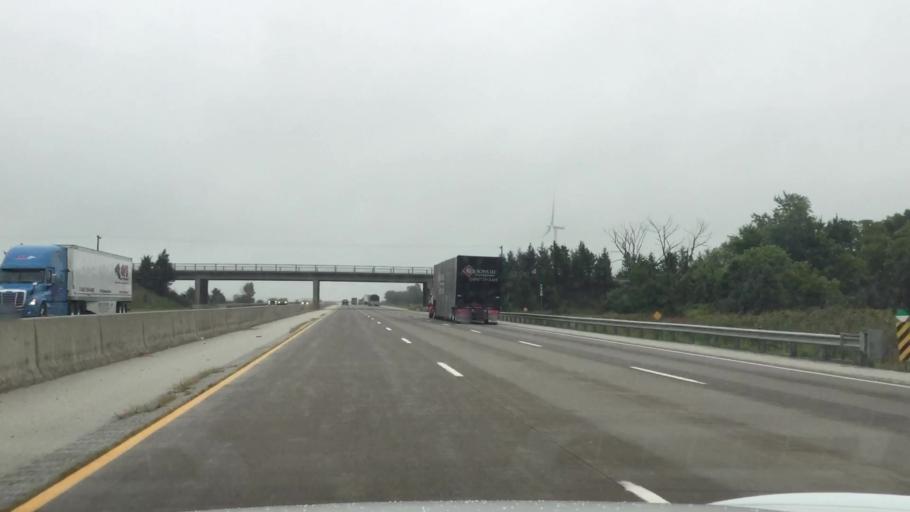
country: US
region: Michigan
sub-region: Wayne County
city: Grosse Pointe Farms
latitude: 42.2360
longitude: -82.6889
